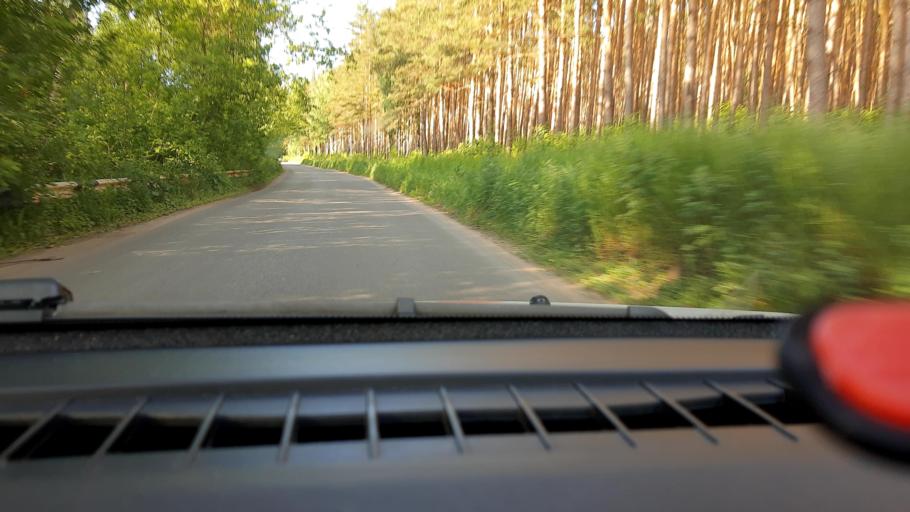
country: RU
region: Nizjnij Novgorod
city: Gorbatovka
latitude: 56.2259
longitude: 43.7608
